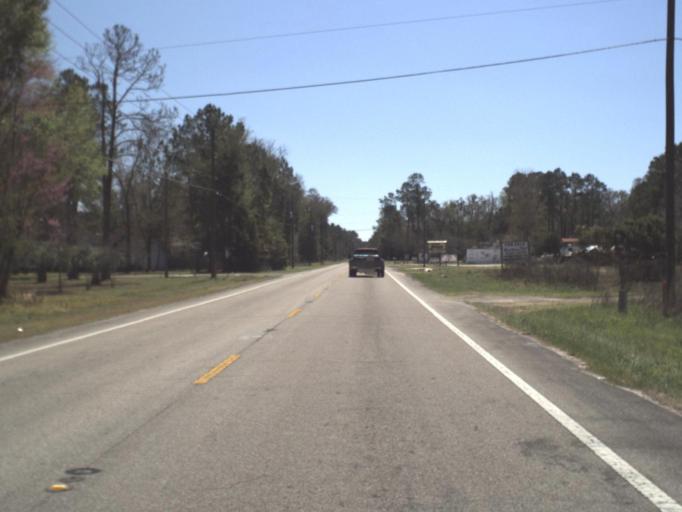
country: US
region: Florida
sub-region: Leon County
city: Woodville
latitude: 30.2464
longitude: -84.2331
